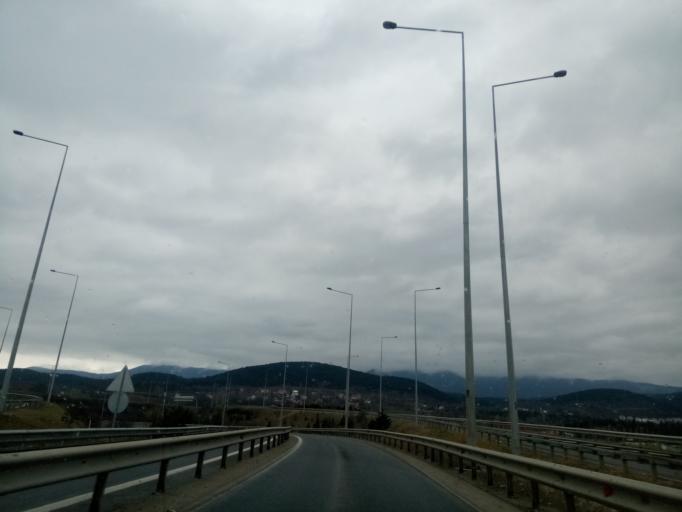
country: TR
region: Bolu
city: Bolu
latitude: 40.7156
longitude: 31.5271
